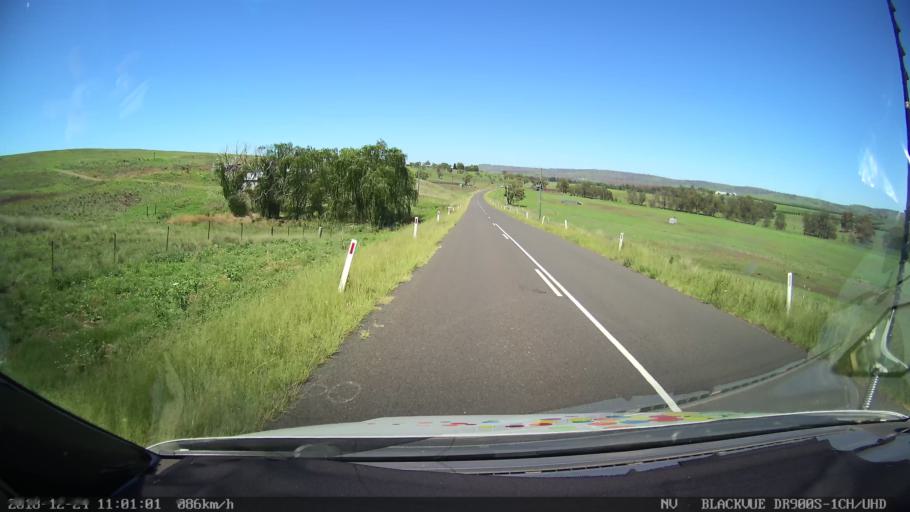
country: AU
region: New South Wales
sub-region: Upper Hunter Shire
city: Merriwa
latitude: -32.0722
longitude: 150.3888
